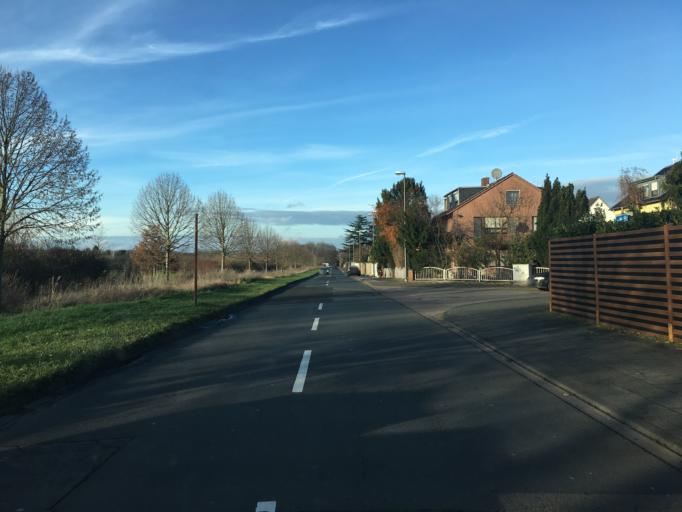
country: DE
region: North Rhine-Westphalia
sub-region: Regierungsbezirk Koln
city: Porz am Rhein
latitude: 50.8764
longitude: 7.0174
